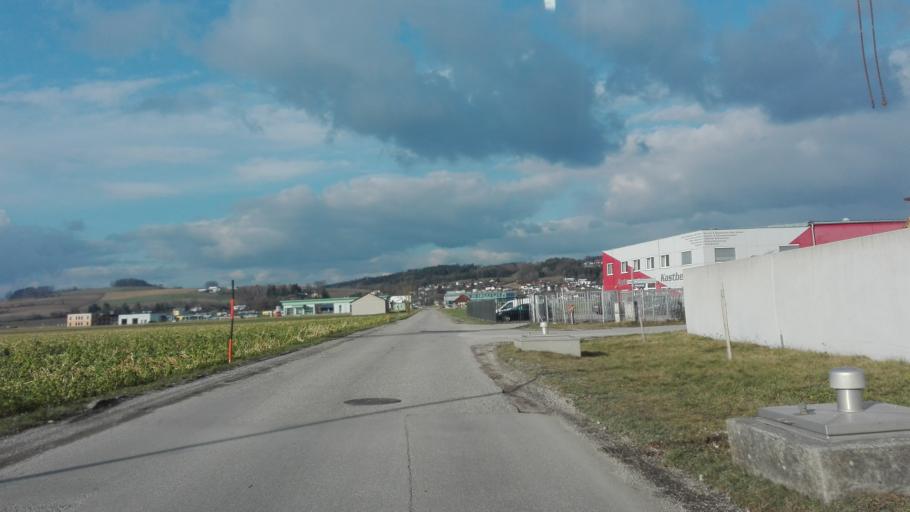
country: AT
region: Upper Austria
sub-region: Politischer Bezirk Perg
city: Perg
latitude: 48.2407
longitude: 14.6204
